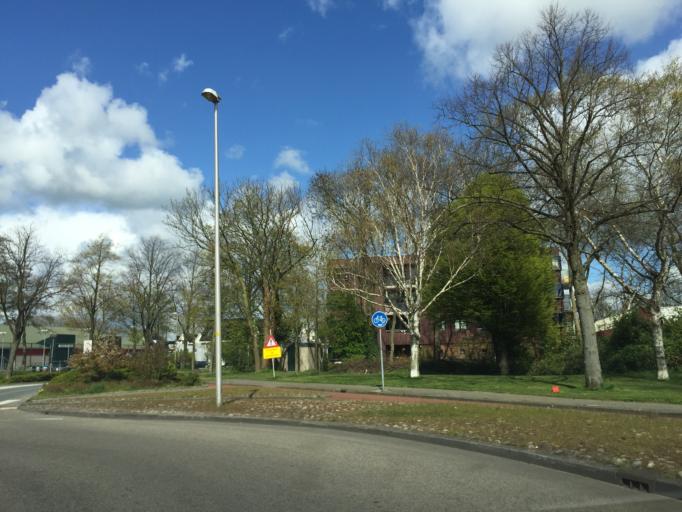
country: NL
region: South Holland
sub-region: Gemeente Leiderdorp
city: Leiderdorp
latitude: 52.1511
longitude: 4.5285
